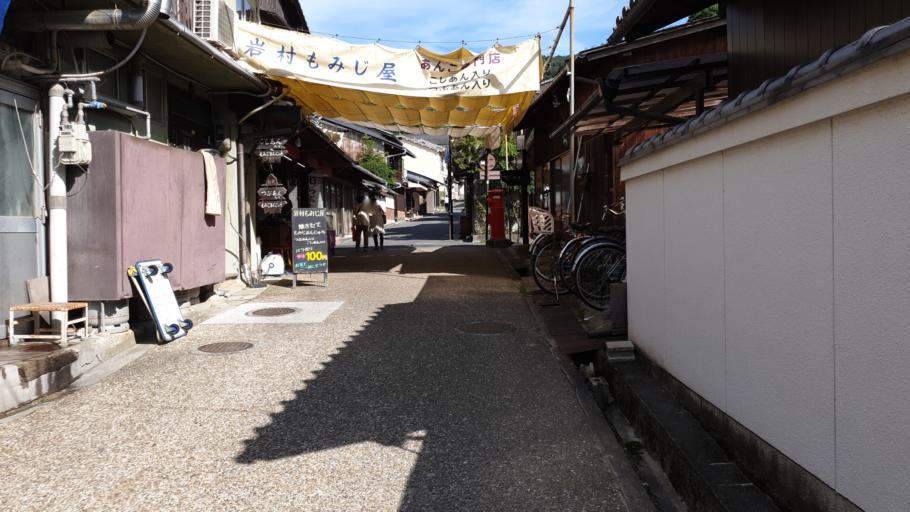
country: JP
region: Hiroshima
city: Miyajima
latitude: 34.2951
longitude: 132.3200
